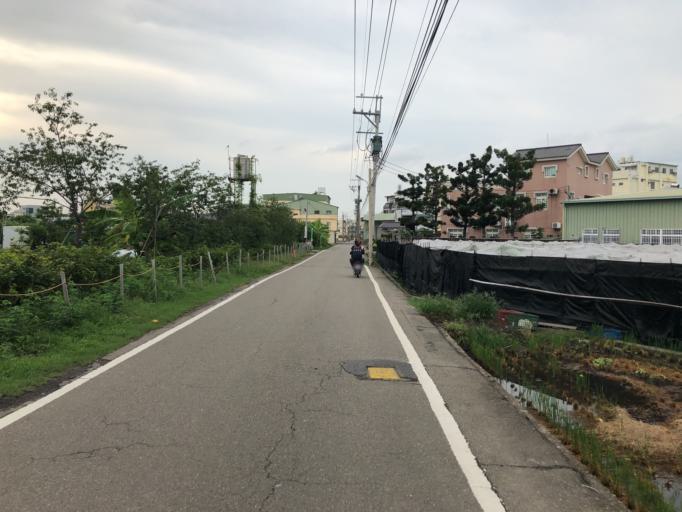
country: TW
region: Taiwan
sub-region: Taichung City
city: Taichung
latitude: 24.0583
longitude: 120.6841
